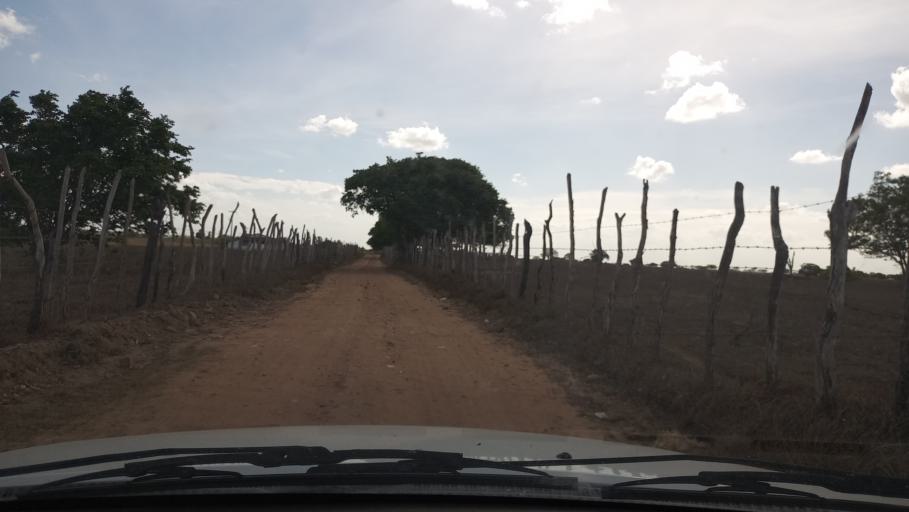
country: BR
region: Rio Grande do Norte
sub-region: Goianinha
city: Goianinha
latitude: -6.3057
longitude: -35.3043
